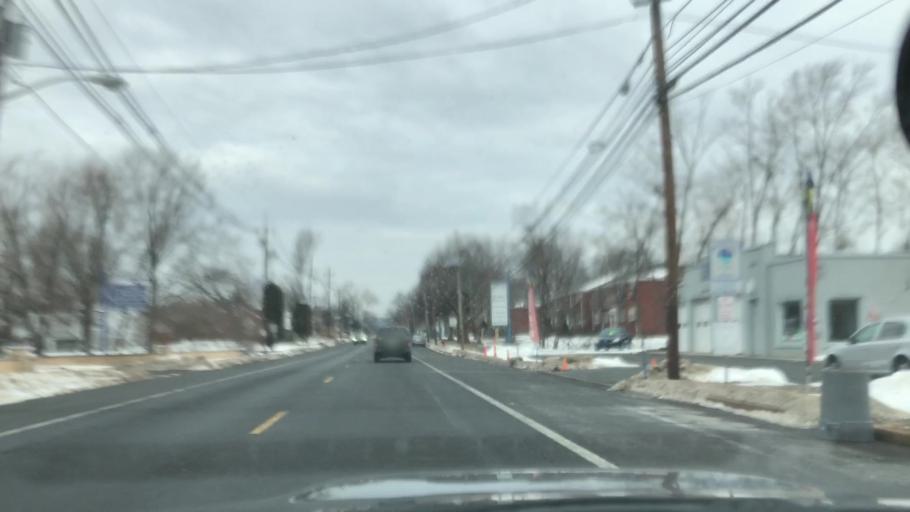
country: US
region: New Jersey
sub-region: Somerset County
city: South Bound Brook
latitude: 40.5468
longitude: -74.5200
